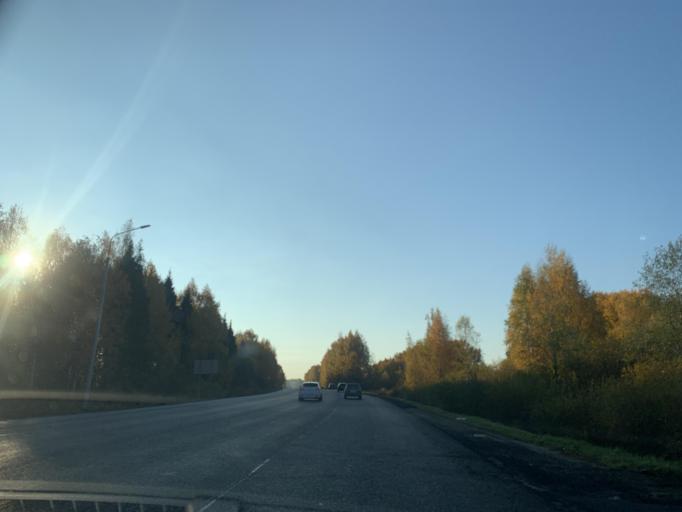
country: RU
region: Jaroslavl
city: Konstantinovskiy
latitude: 57.8061
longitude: 39.5881
